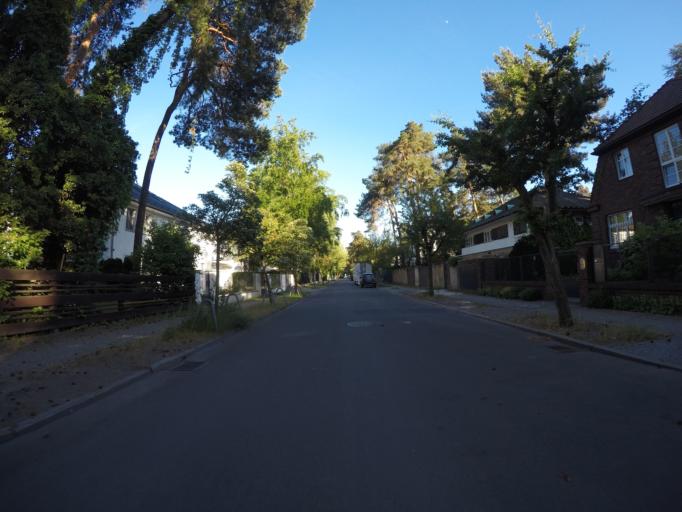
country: DE
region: Berlin
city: Schmargendorf
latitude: 52.4685
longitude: 13.2816
